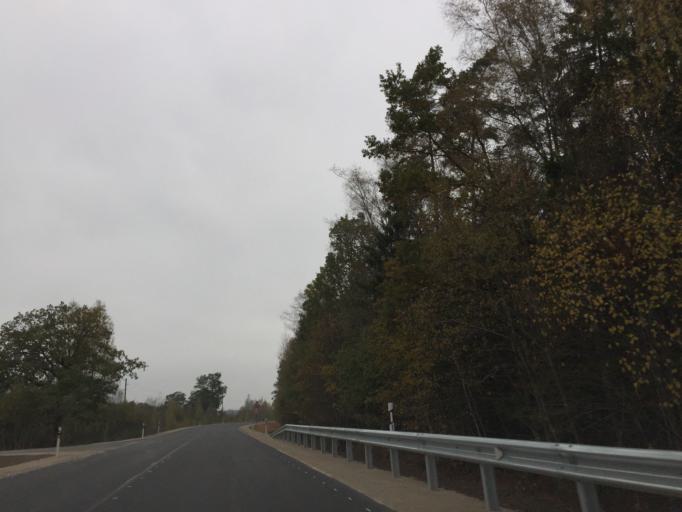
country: LV
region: Jelgava
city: Jelgava
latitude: 56.6613
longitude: 23.5685
